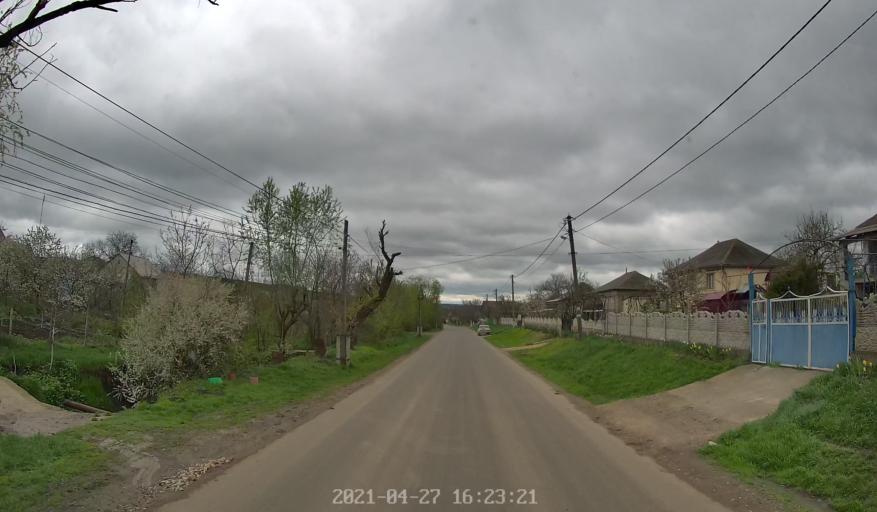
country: MD
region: Chisinau
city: Singera
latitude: 46.9993
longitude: 29.0173
